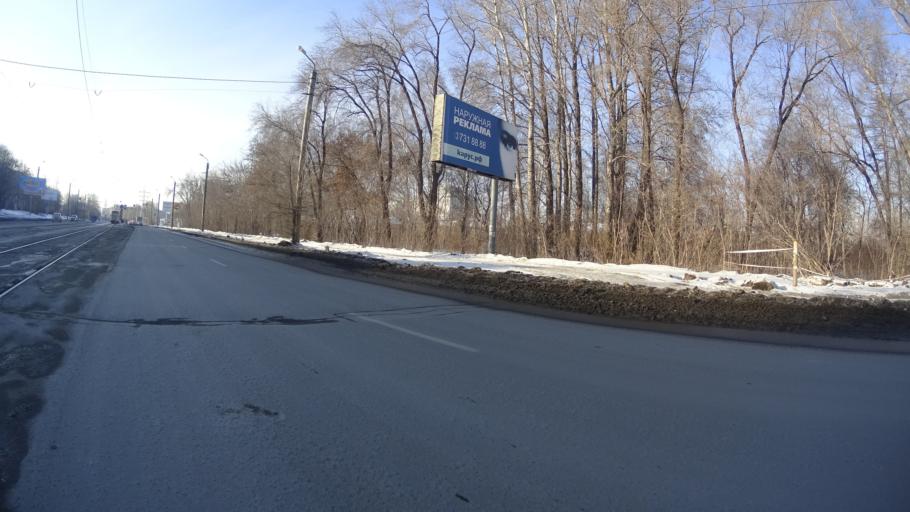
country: RU
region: Chelyabinsk
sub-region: Gorod Chelyabinsk
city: Chelyabinsk
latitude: 55.1679
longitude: 61.4387
